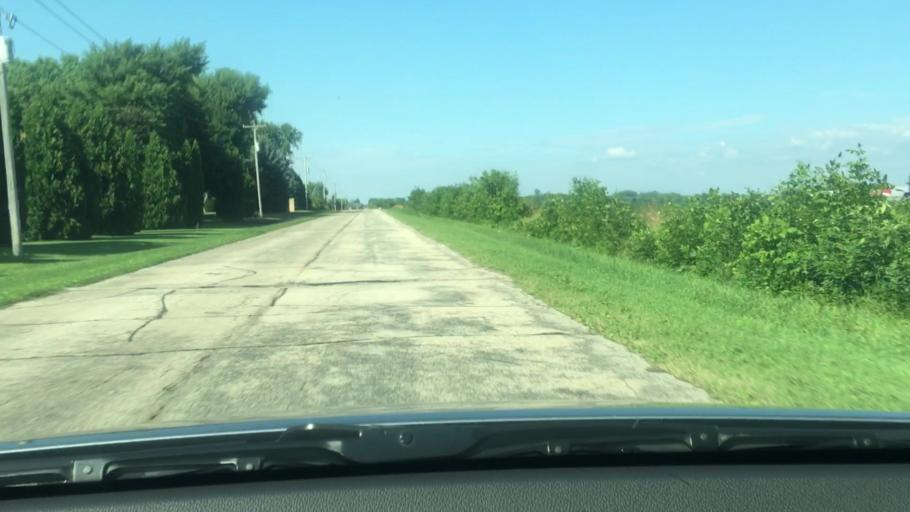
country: US
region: Wisconsin
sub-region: Winnebago County
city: Oshkosh
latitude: 43.9560
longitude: -88.5781
